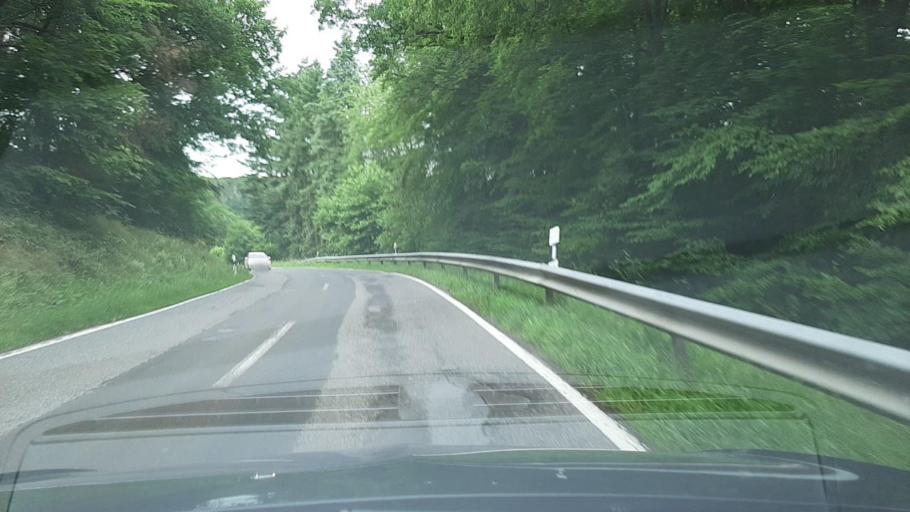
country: DE
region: Rheinland-Pfalz
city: Roth
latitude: 50.0914
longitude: 7.4524
